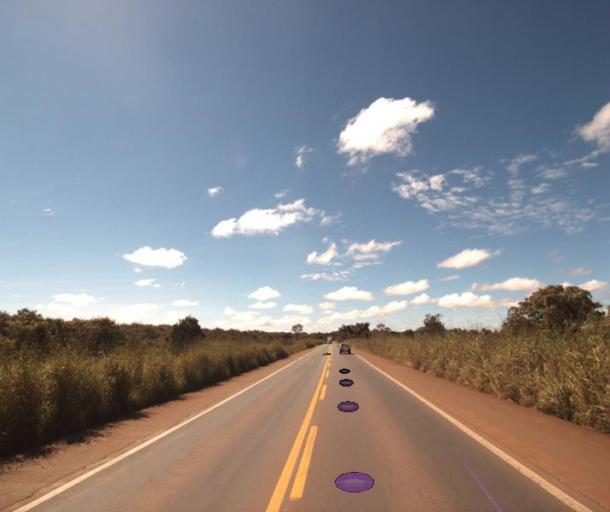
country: BR
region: Goias
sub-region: Rialma
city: Rialma
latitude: -15.3954
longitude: -49.5450
